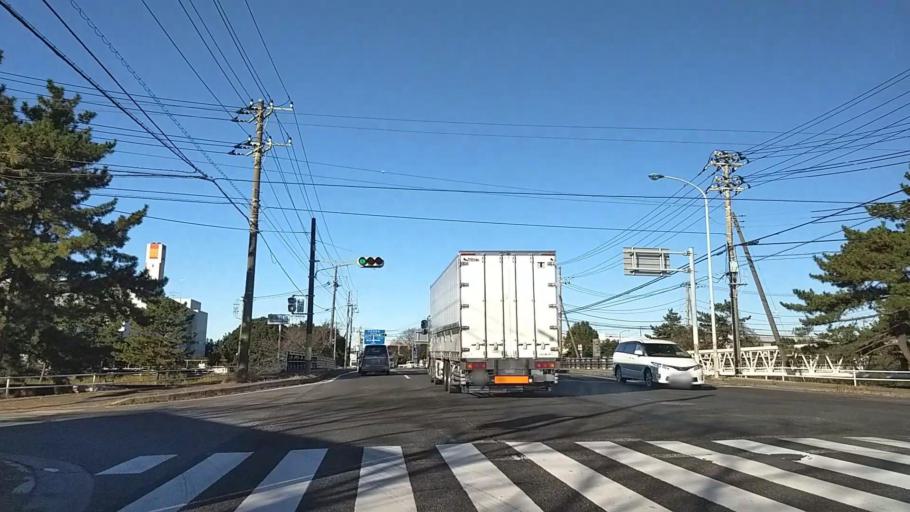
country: JP
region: Chiba
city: Kisarazu
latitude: 35.3704
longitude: 139.9137
